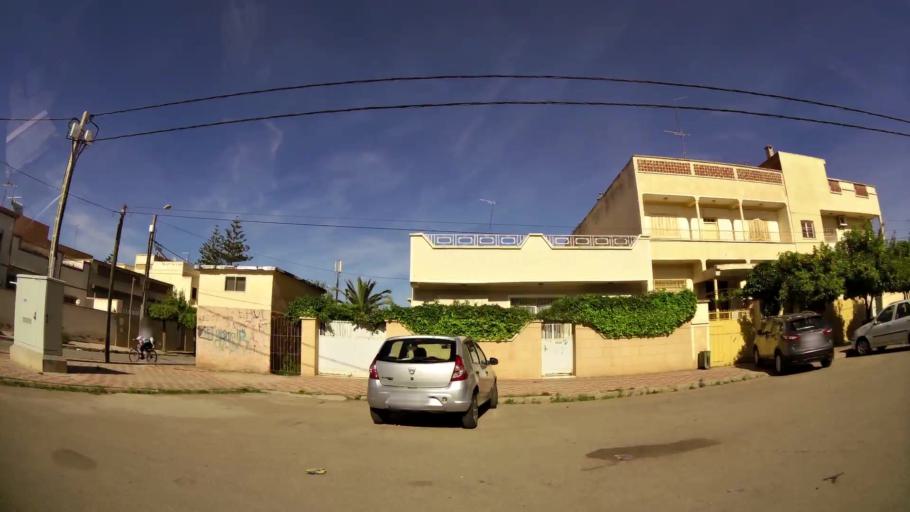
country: MA
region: Oriental
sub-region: Oujda-Angad
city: Oujda
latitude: 34.6668
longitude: -1.9079
